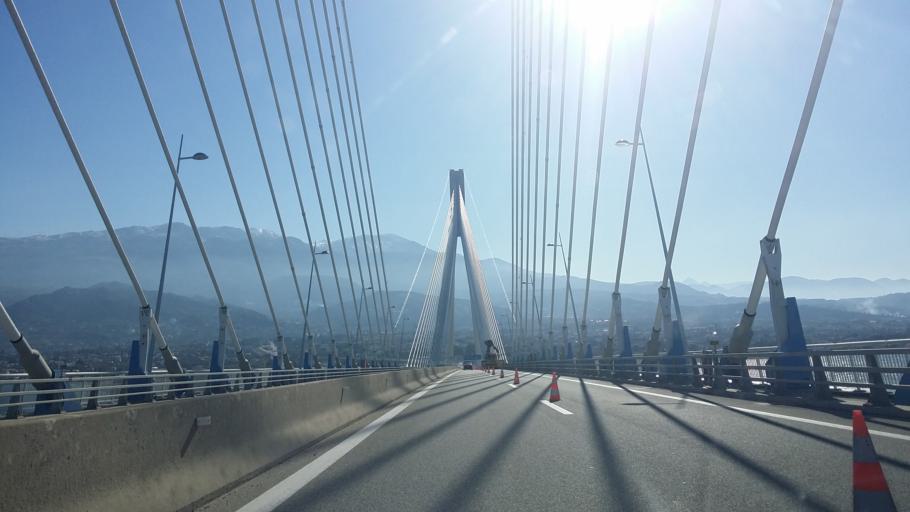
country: GR
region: West Greece
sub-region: Nomos Aitolias kai Akarnanias
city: Antirrio
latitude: 38.3175
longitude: 21.7753
